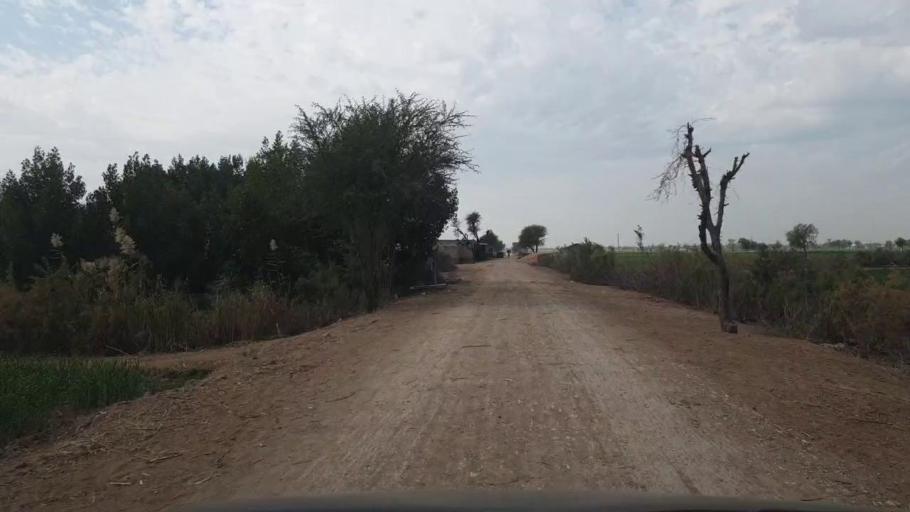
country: PK
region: Sindh
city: Sakrand
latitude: 26.0092
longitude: 68.3800
